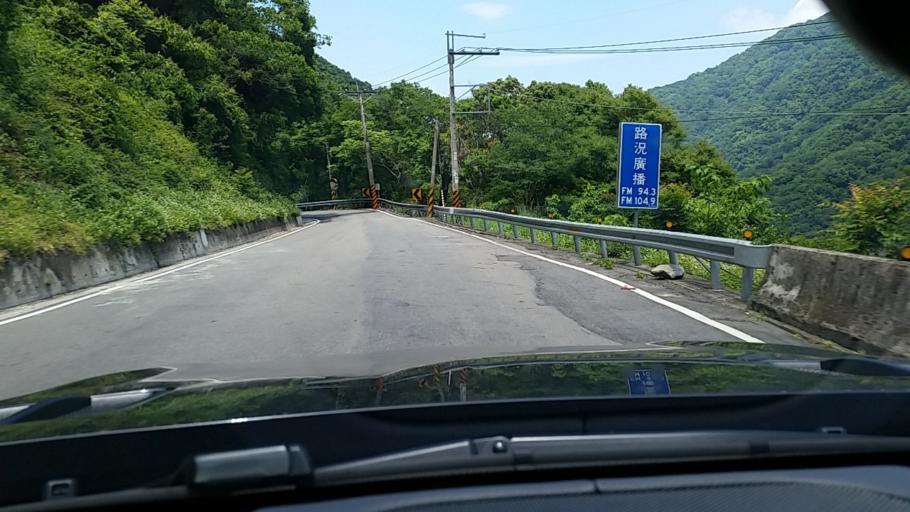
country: TW
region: Taiwan
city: Daxi
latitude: 24.6984
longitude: 121.3657
